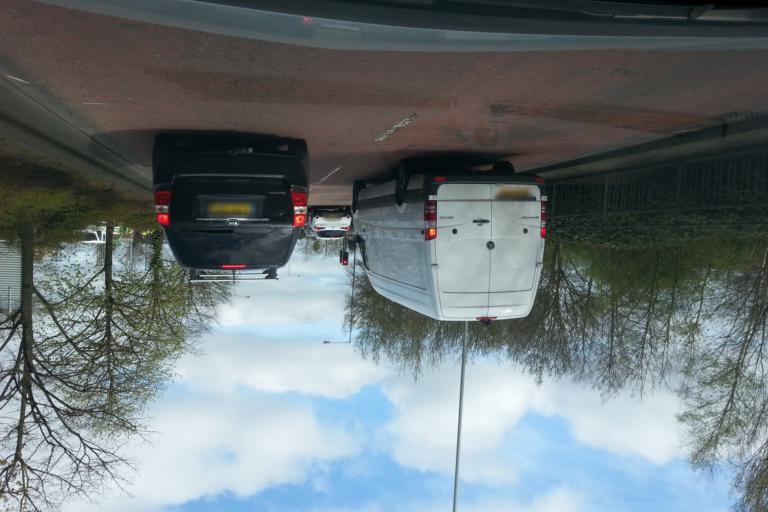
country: GB
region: England
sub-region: Wolverhampton
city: Bilston
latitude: 52.5648
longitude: -2.0724
